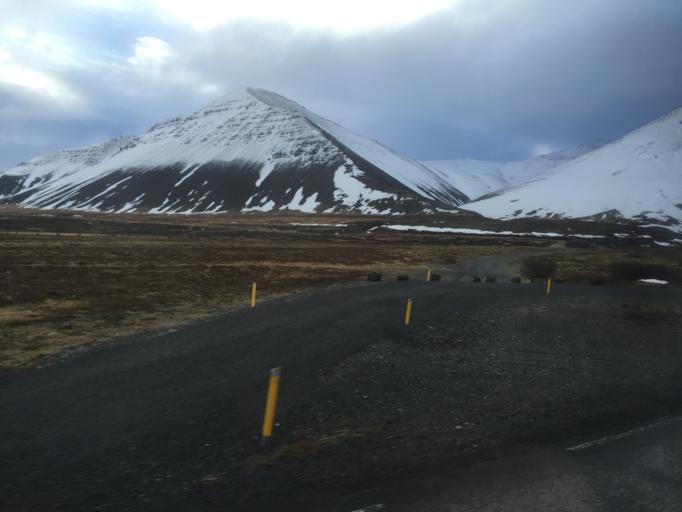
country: IS
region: West
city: Borgarnes
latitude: 64.5226
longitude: -21.8861
